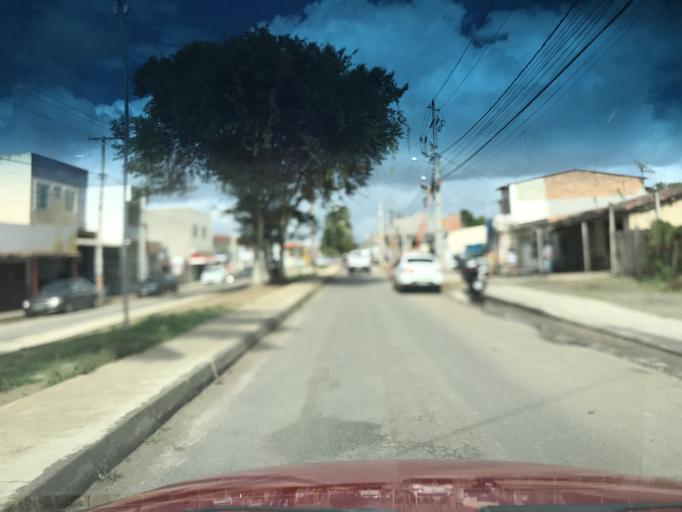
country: BR
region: Bahia
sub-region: Santo Antonio De Jesus
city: Santo Antonio de Jesus
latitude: -12.9738
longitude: -39.2735
